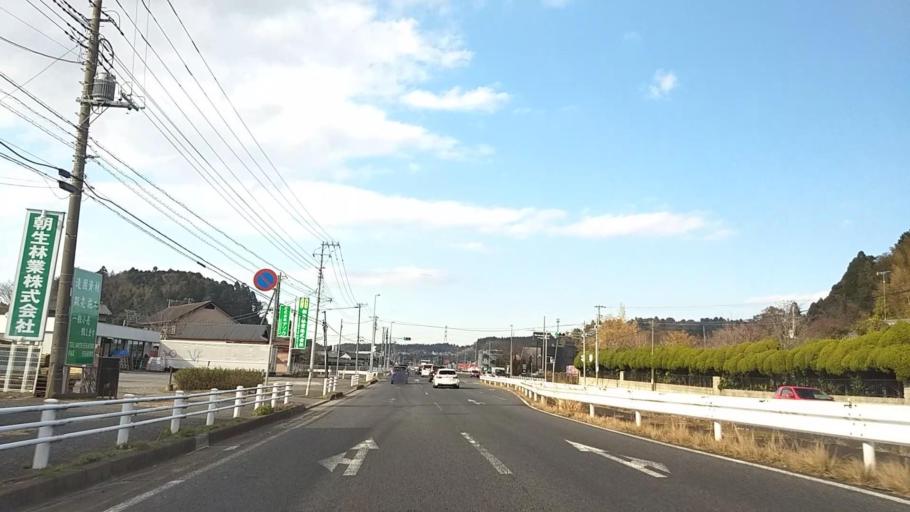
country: JP
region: Chiba
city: Togane
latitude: 35.5671
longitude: 140.3348
